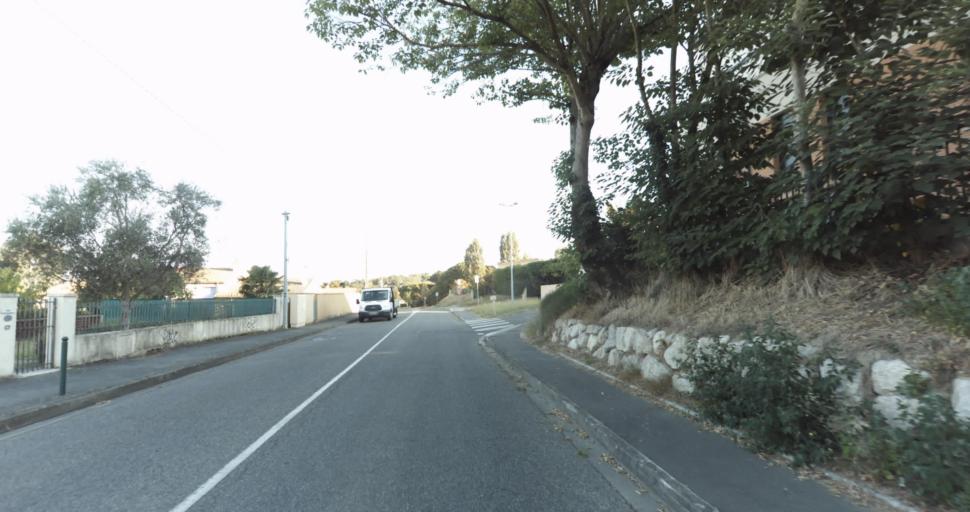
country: FR
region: Midi-Pyrenees
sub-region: Departement de la Haute-Garonne
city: L'Union
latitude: 43.6620
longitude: 1.4750
